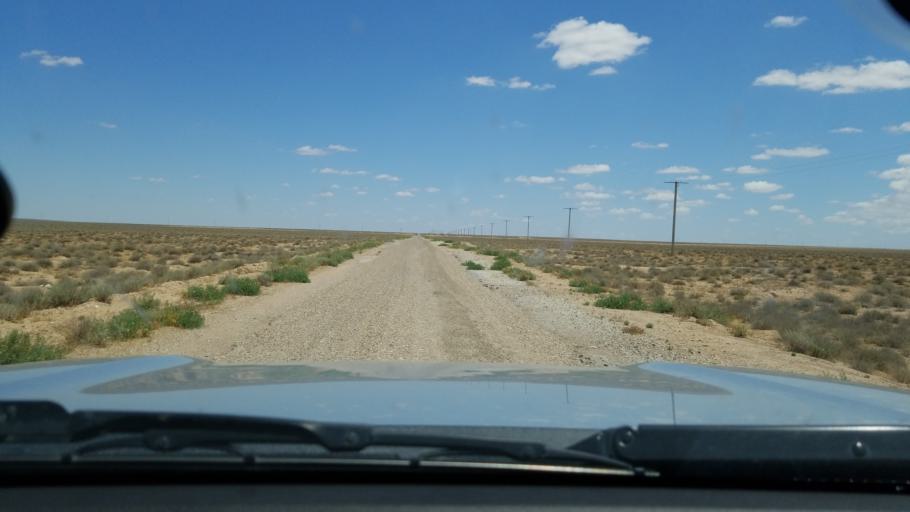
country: TM
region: Balkan
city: Turkmenbasy
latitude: 40.1445
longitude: 53.5724
